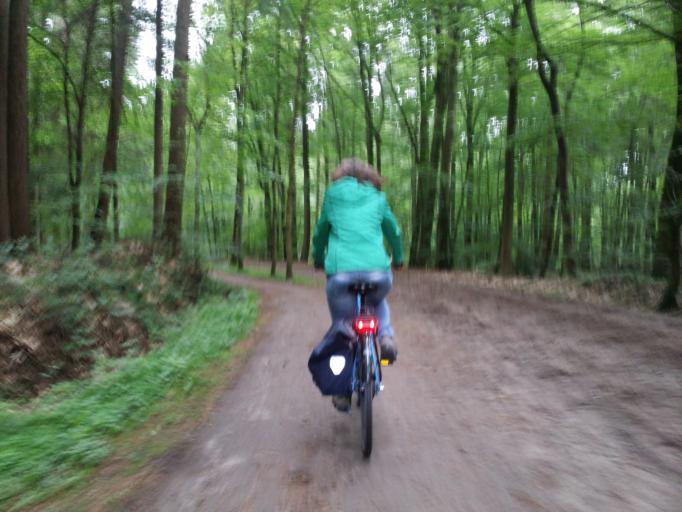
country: DE
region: Lower Saxony
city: Rastede
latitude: 53.2361
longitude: 8.2353
